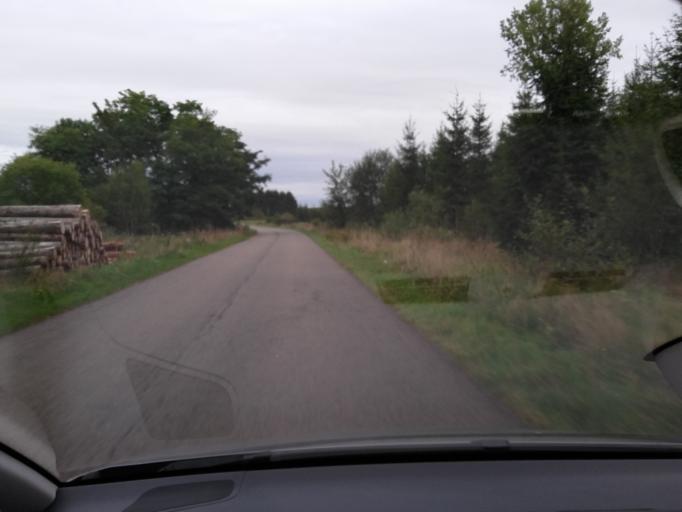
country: BE
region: Wallonia
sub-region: Province du Luxembourg
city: Etalle
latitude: 49.6573
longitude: 5.5808
